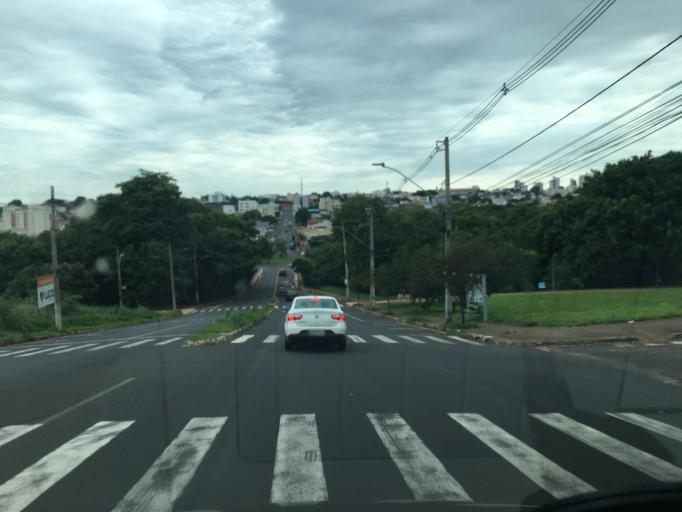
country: BR
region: Minas Gerais
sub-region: Uberlandia
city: Uberlandia
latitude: -18.9215
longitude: -48.3039
